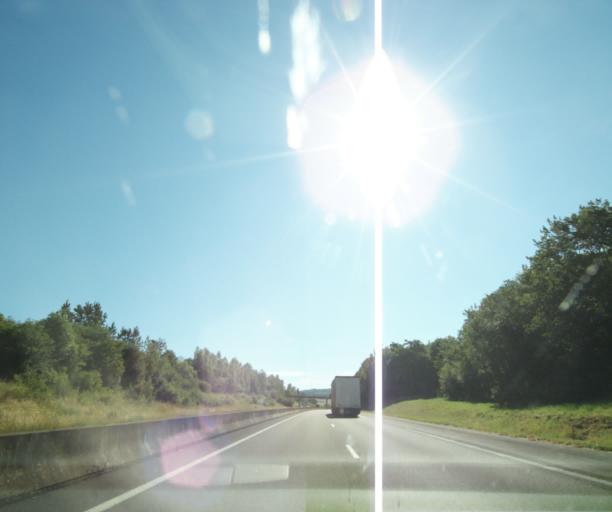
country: FR
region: Champagne-Ardenne
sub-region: Departement de la Haute-Marne
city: Nogent-le-Bas
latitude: 47.9582
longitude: 5.3924
